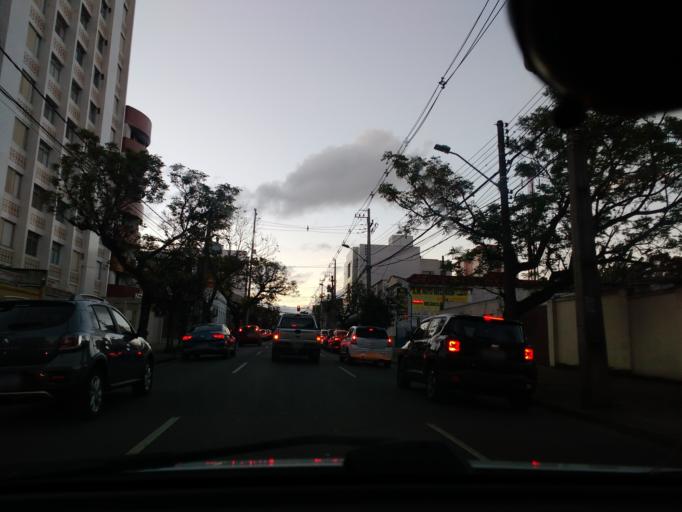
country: BR
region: Parana
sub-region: Curitiba
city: Curitiba
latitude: -25.4336
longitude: -49.2823
